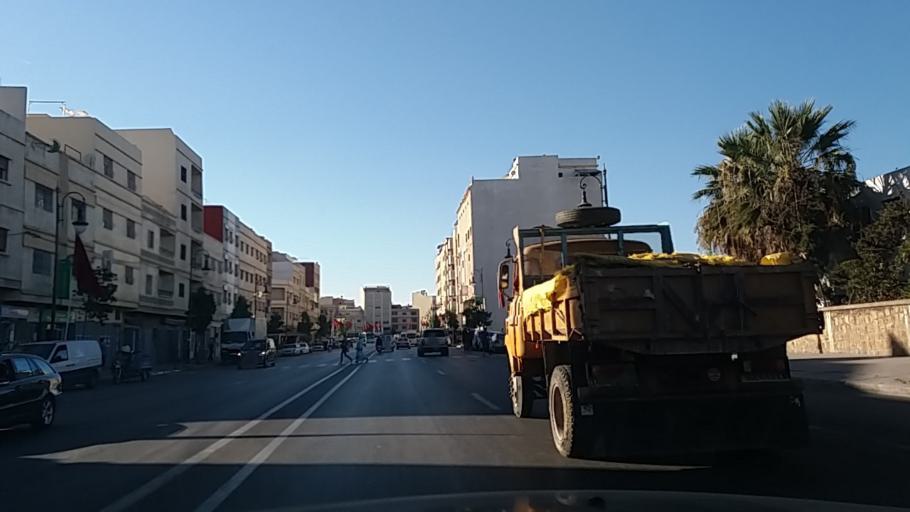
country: MA
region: Tanger-Tetouan
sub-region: Tanger-Assilah
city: Tangier
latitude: 35.7499
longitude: -5.7991
